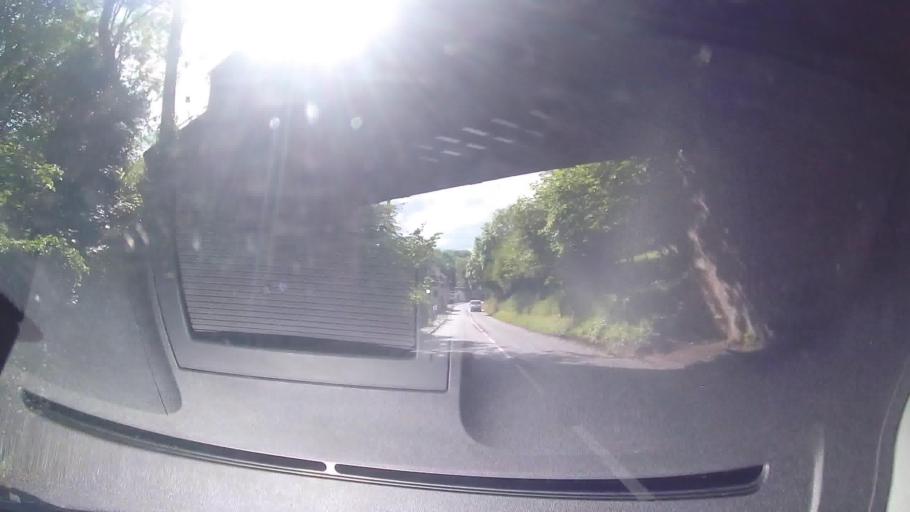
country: GB
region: England
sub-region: Telford and Wrekin
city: Ironbridge
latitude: 52.6318
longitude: -2.5009
